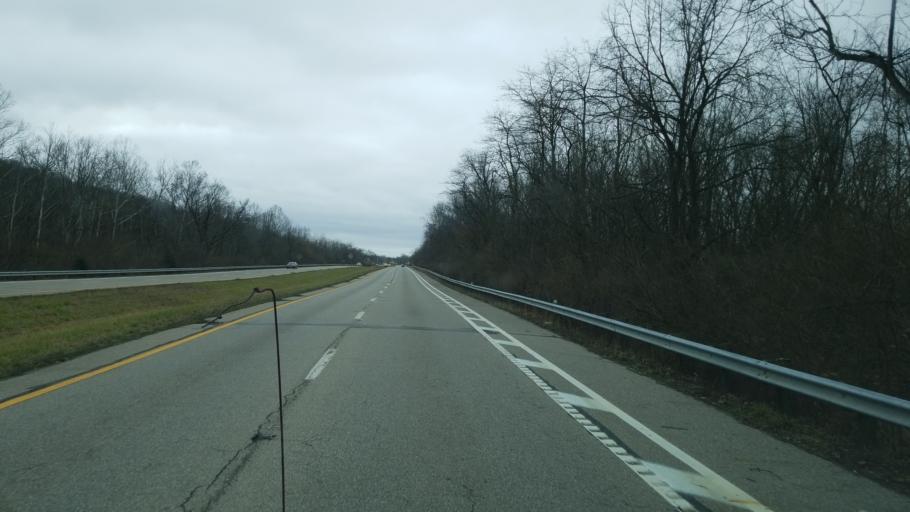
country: US
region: Ohio
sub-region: Clermont County
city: New Richmond
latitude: 38.9633
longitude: -84.2852
